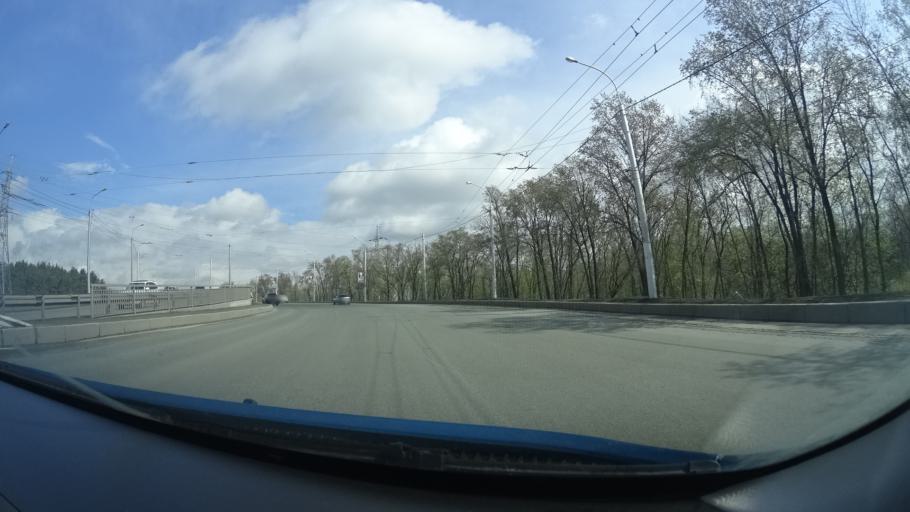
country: RU
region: Bashkortostan
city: Ufa
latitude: 54.8056
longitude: 56.0494
